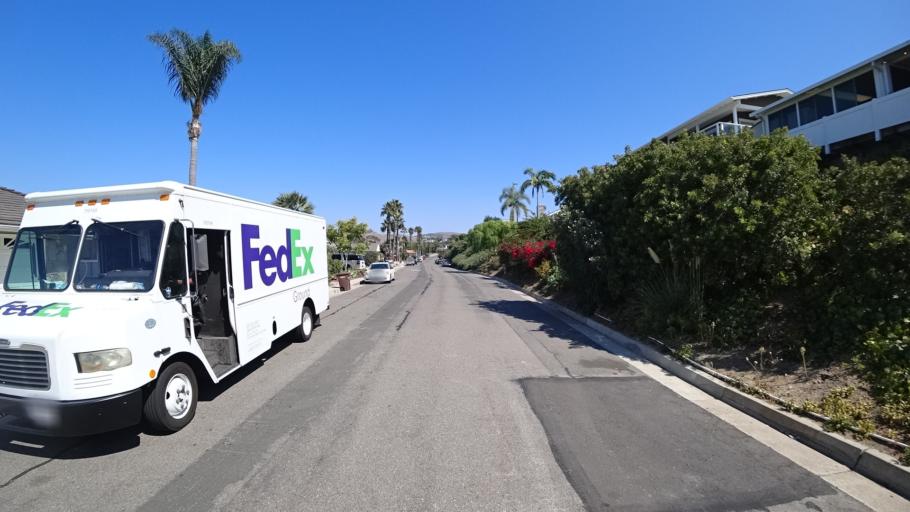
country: US
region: California
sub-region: Orange County
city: San Clemente
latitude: 33.4437
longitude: -117.6368
